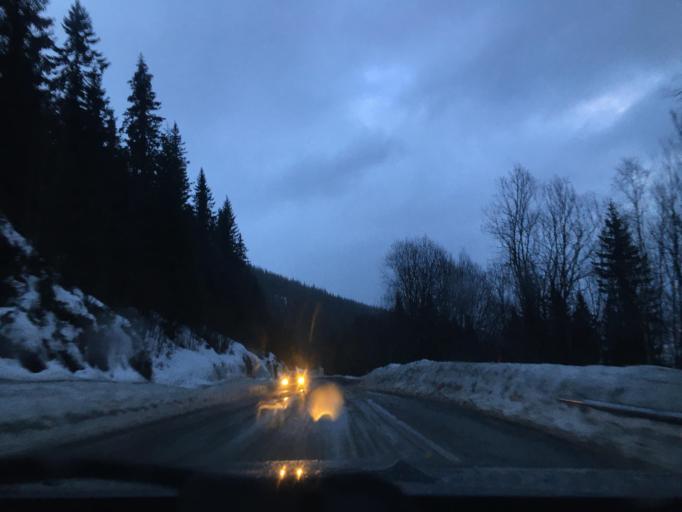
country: NO
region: Nordland
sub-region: Rana
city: Hauknes
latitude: 66.2838
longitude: 13.9062
